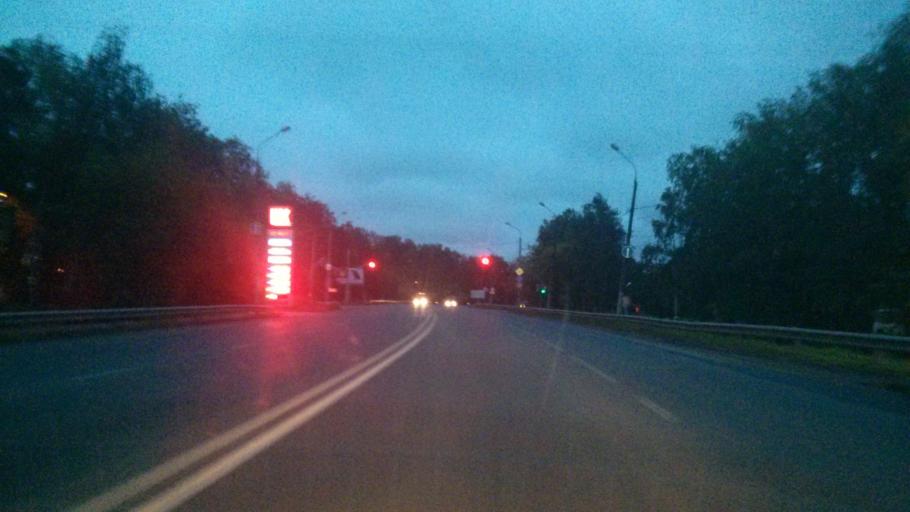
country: RU
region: Nizjnij Novgorod
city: Nizhniy Novgorod
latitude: 56.2239
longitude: 43.9400
